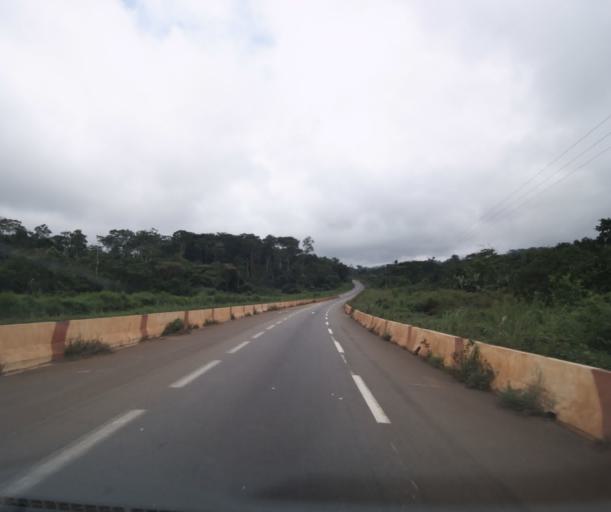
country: CM
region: Centre
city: Mbankomo
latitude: 3.7956
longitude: 11.3680
